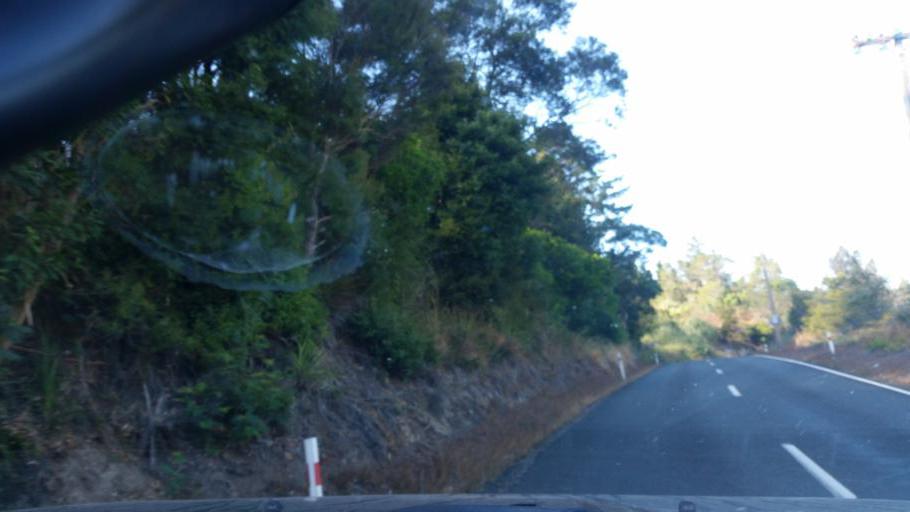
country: NZ
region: Northland
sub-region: Kaipara District
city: Dargaville
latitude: -35.8123
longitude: 173.7275
